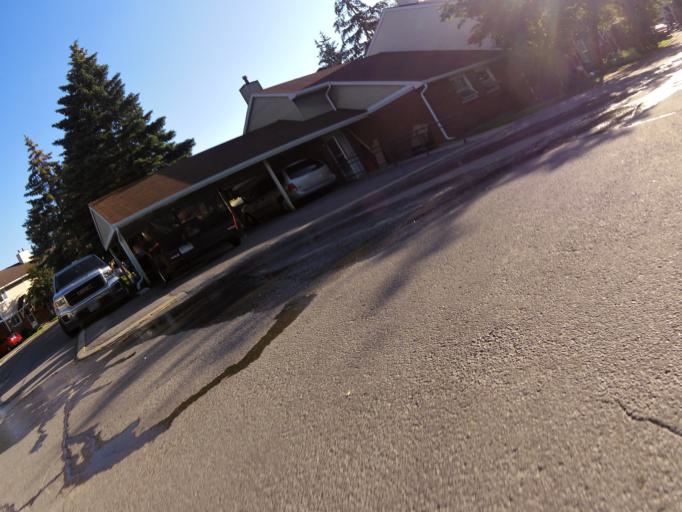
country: CA
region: Ontario
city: Bells Corners
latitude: 45.3439
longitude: -75.7907
